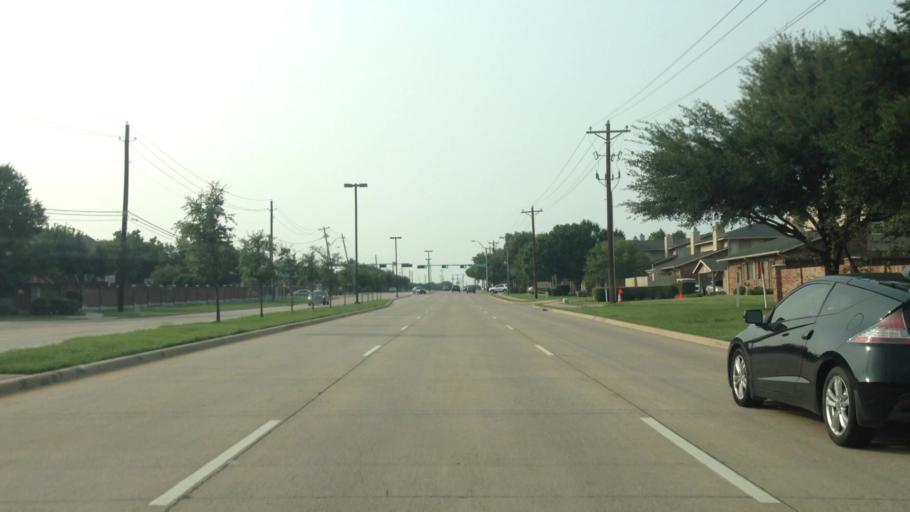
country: US
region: Texas
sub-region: Dallas County
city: Carrollton
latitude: 33.0141
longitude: -96.9127
